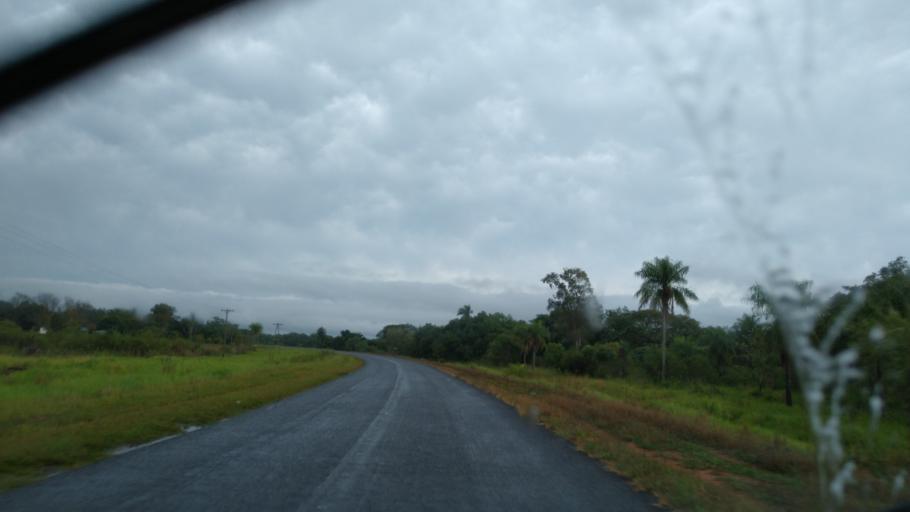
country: AR
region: Corrientes
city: Loreto
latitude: -27.7746
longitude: -57.2703
